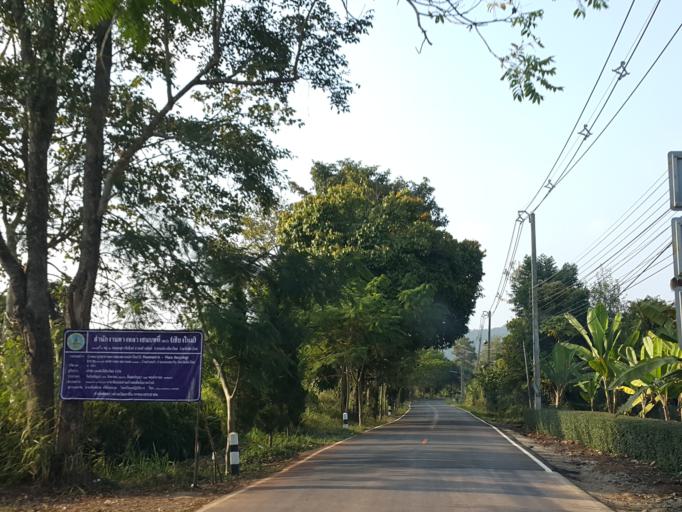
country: TH
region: Chiang Mai
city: Mae On
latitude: 18.8653
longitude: 99.2723
